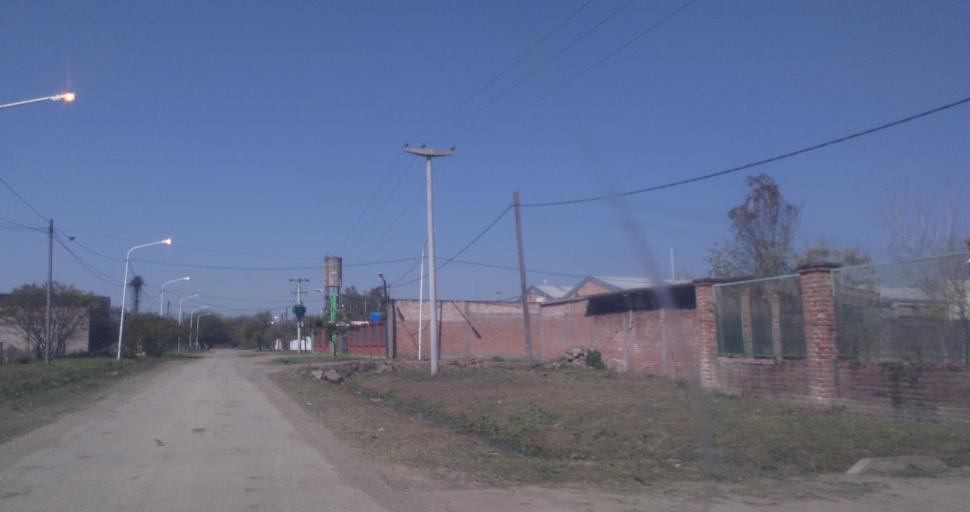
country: AR
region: Chaco
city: Fontana
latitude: -27.4330
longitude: -59.0290
